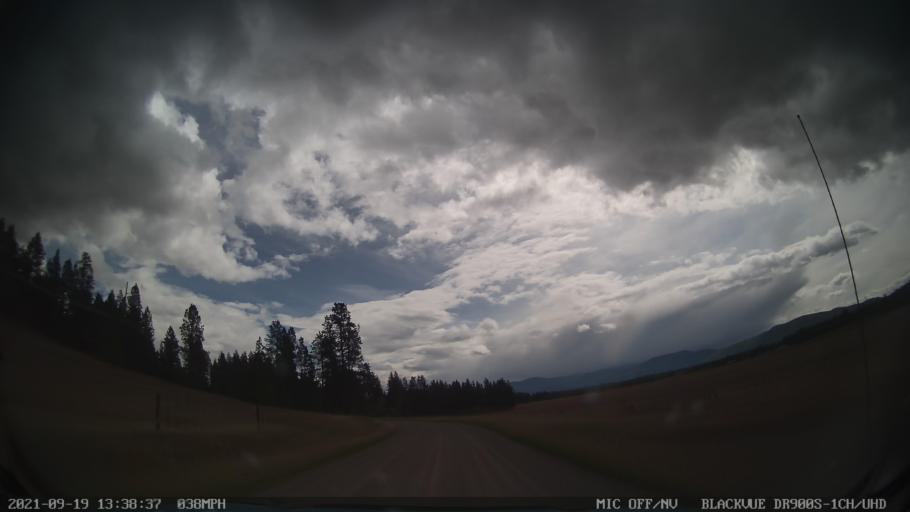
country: US
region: Montana
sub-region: Missoula County
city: Seeley Lake
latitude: 47.1035
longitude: -113.2701
